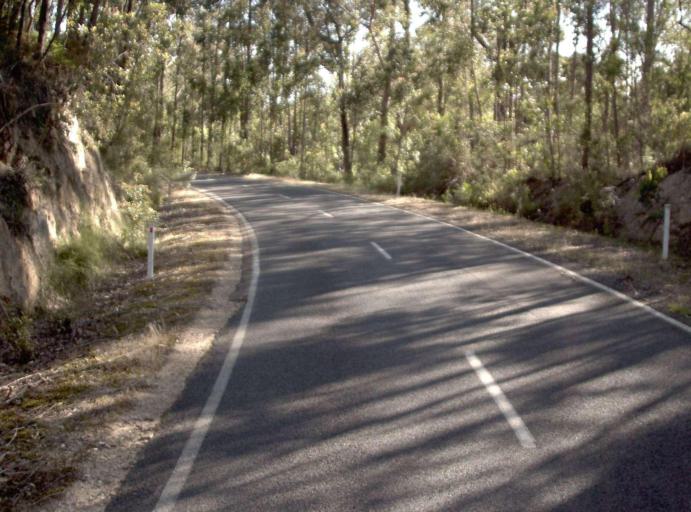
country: AU
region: Victoria
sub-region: East Gippsland
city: Lakes Entrance
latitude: -37.6516
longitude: 148.4788
